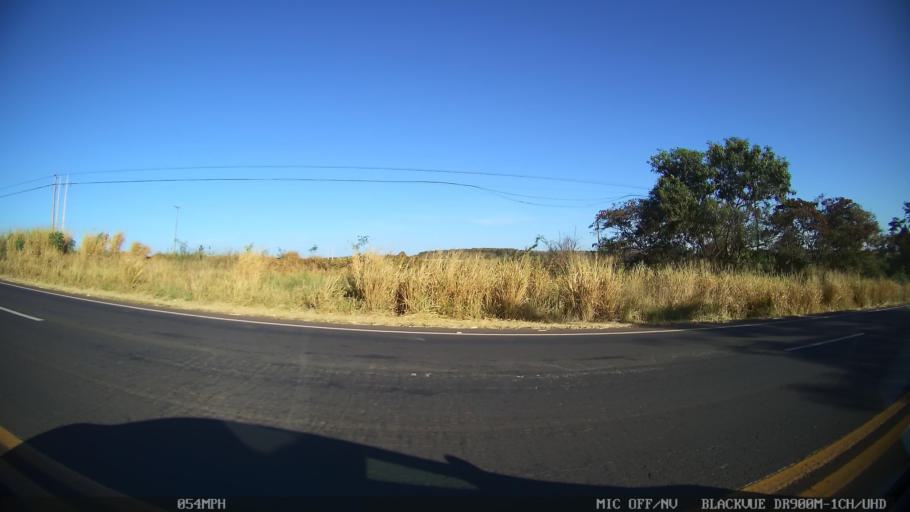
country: BR
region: Sao Paulo
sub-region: Olimpia
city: Olimpia
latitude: -20.7014
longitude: -48.9406
